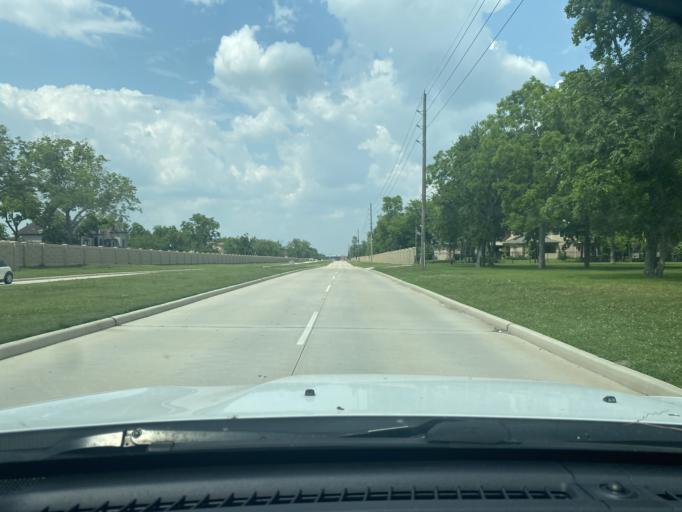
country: US
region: Texas
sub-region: Fort Bend County
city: Greatwood
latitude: 29.5473
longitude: -95.7214
